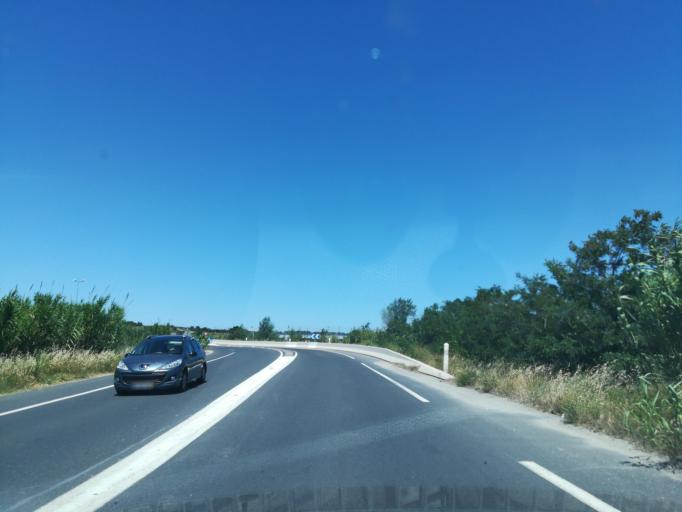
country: FR
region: Languedoc-Roussillon
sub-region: Departement des Pyrenees-Orientales
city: el Volo
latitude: 42.5433
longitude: 2.8503
